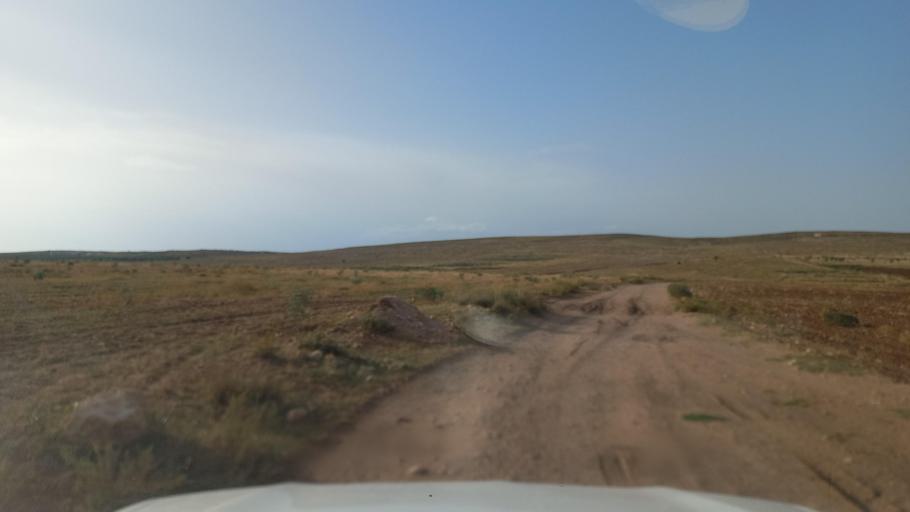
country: TN
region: Al Qasrayn
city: Kasserine
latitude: 35.3554
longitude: 8.8419
